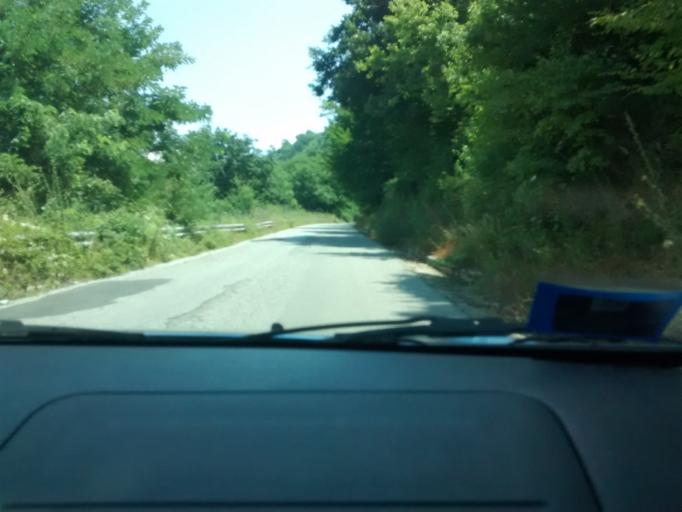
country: IT
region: Calabria
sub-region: Provincia di Catanzaro
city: Maida
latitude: 38.8999
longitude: 16.3856
